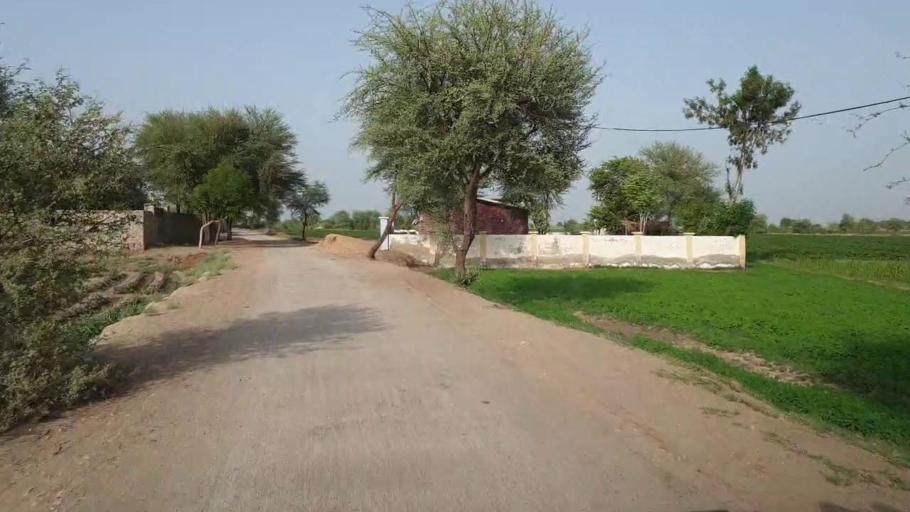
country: PK
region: Sindh
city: Daur
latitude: 26.3399
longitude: 68.2557
